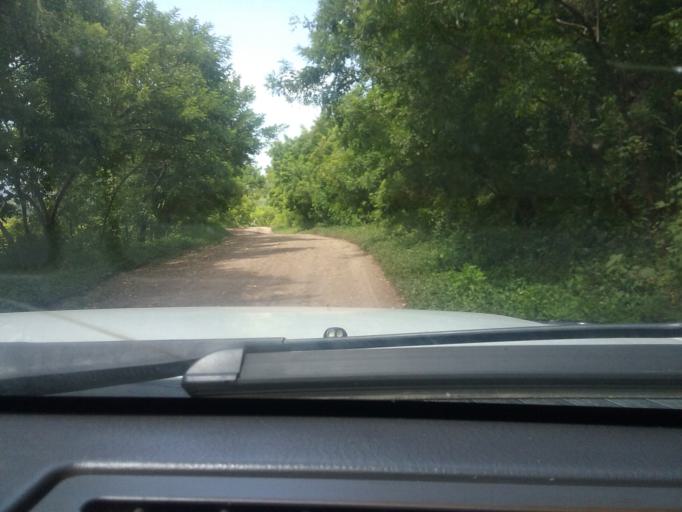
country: NI
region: Matagalpa
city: Terrabona
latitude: 12.6969
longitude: -85.9508
